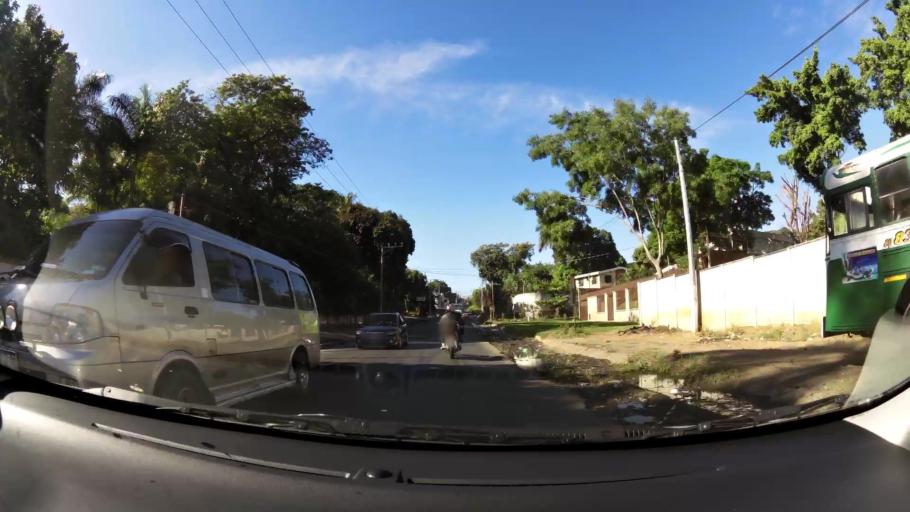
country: SV
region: Santa Ana
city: Santa Ana
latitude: 13.9871
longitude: -89.5672
